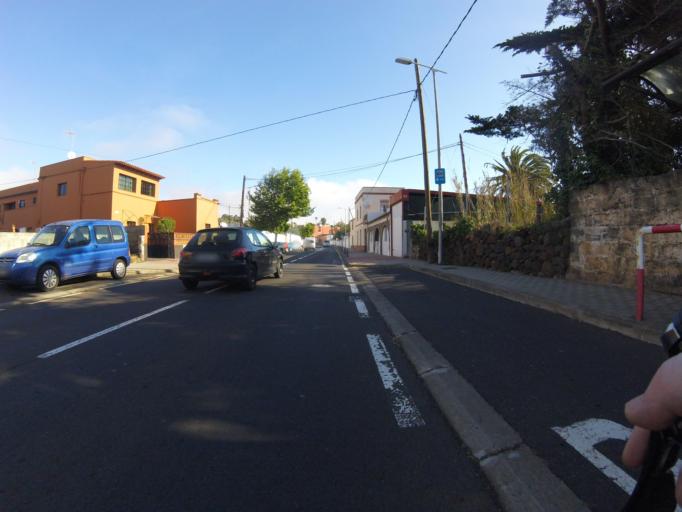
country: ES
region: Canary Islands
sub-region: Provincia de Santa Cruz de Tenerife
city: La Laguna
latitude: 28.4653
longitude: -16.3163
